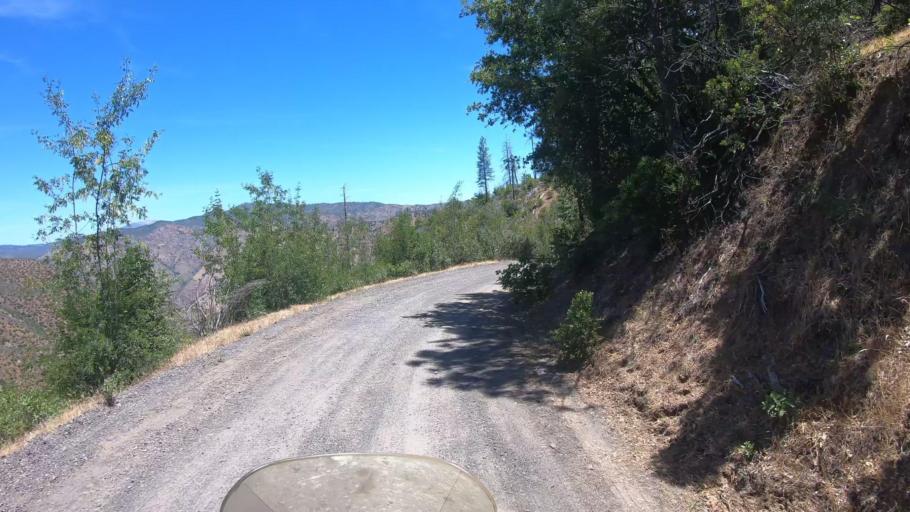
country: US
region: California
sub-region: Tuolumne County
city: Tuolumne City
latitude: 37.8318
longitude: -120.1132
